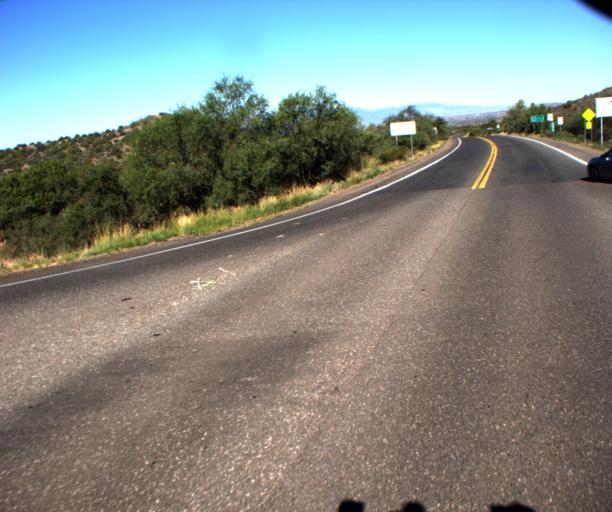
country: US
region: Arizona
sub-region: Yavapai County
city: Lake Montezuma
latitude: 34.6904
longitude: -111.7438
